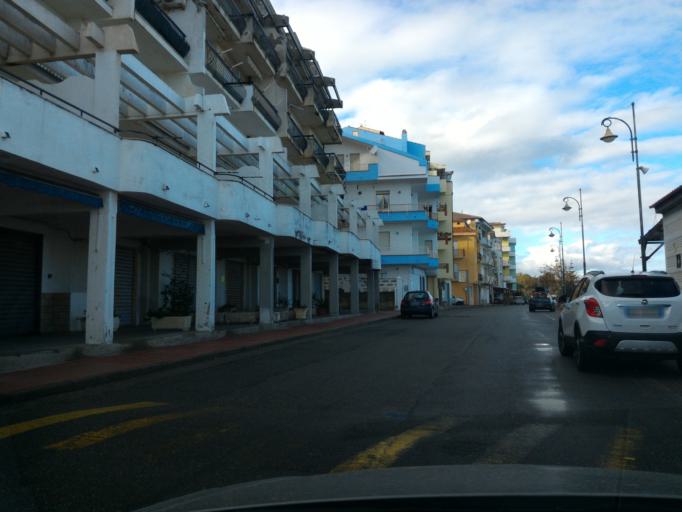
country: IT
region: Calabria
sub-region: Provincia di Crotone
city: Torretta
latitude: 39.4522
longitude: 17.0395
